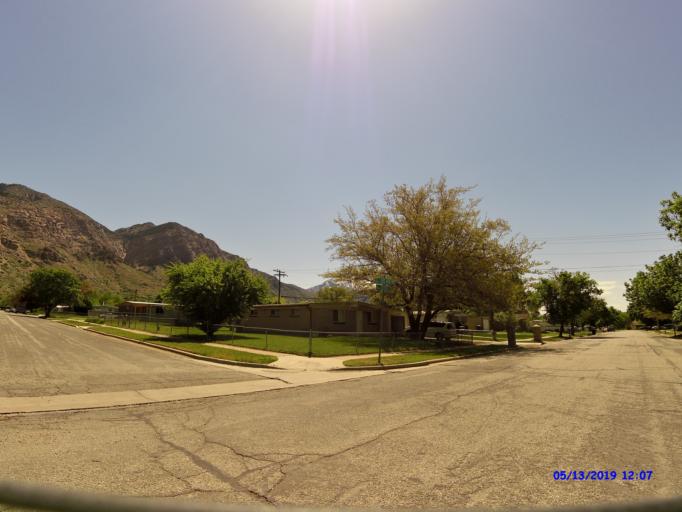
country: US
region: Utah
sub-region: Weber County
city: Harrisville
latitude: 41.2764
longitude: -111.9640
